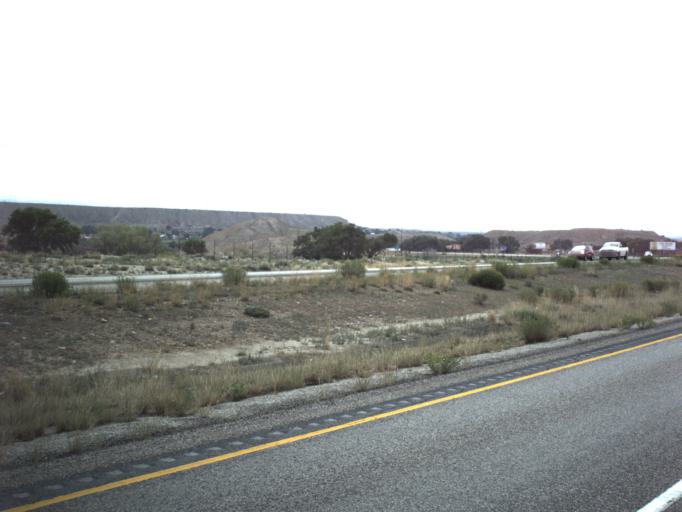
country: US
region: Utah
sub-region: Carbon County
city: Carbonville
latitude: 39.6189
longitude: -110.8550
